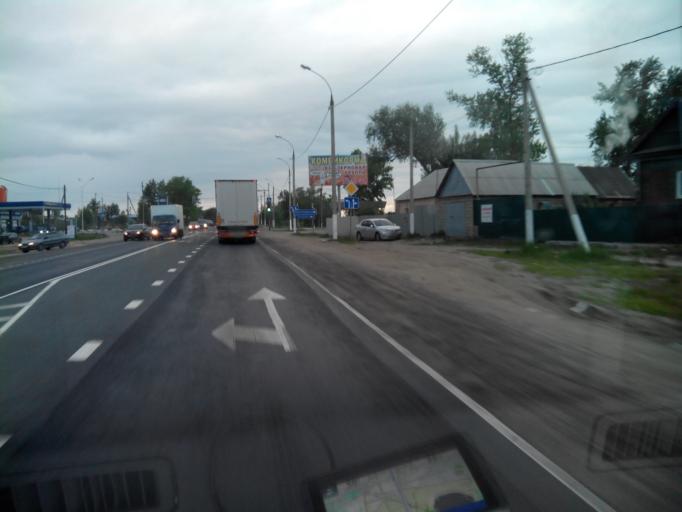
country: RU
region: Penza
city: Chemodanovka
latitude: 53.2212
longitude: 45.2324
